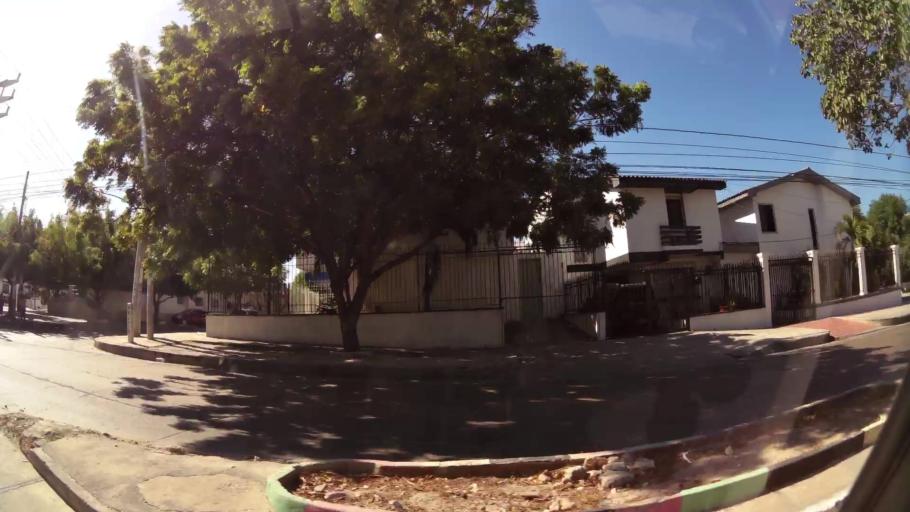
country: CO
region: Atlantico
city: Barranquilla
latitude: 10.9972
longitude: -74.7912
